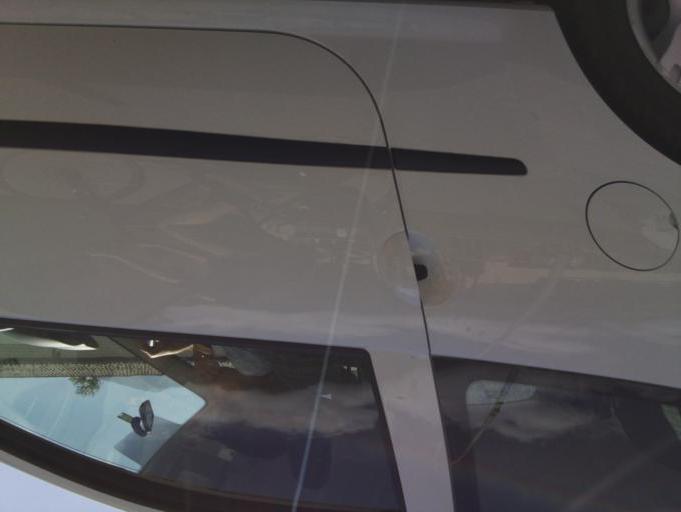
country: CH
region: Glarus
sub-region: Glarus
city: Netstal
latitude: 47.0602
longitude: 9.0527
